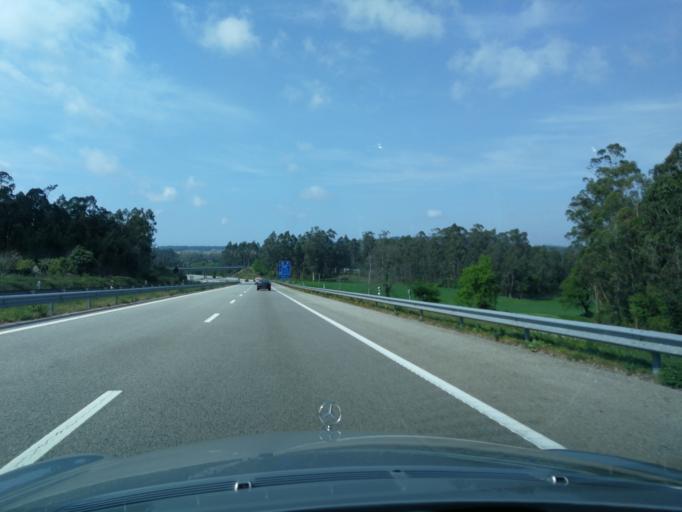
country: PT
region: Porto
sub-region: Vila do Conde
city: Arvore
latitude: 41.3885
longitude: -8.6706
